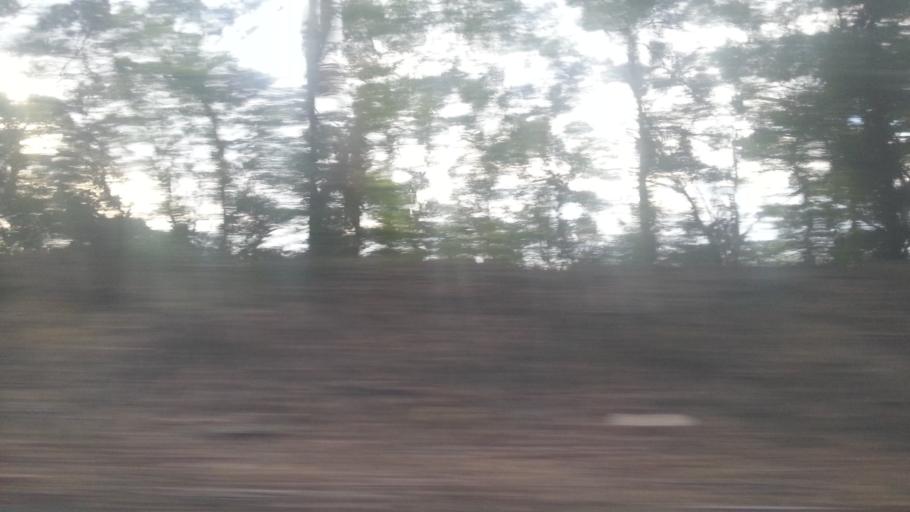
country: AU
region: New South Wales
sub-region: Wollongong
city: Mount Ousley
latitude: -34.3858
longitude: 150.8547
